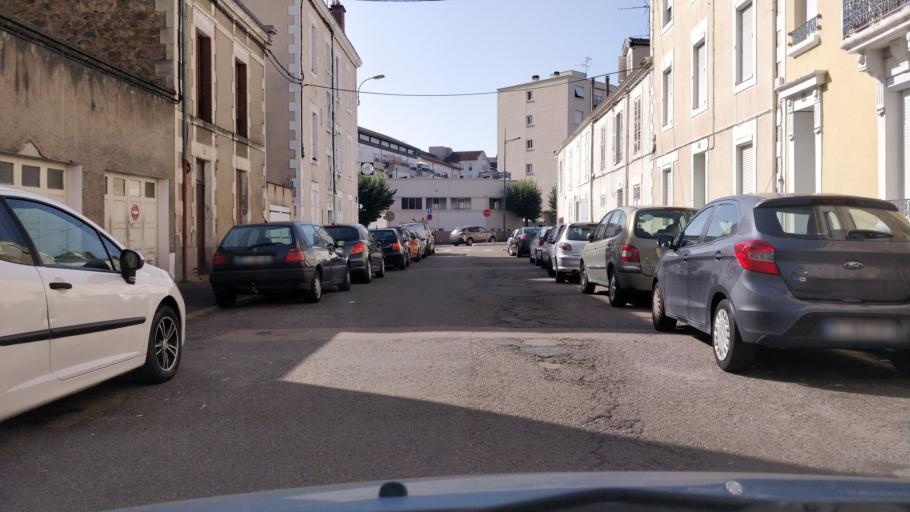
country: FR
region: Limousin
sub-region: Departement de la Haute-Vienne
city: Limoges
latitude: 45.8396
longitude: 1.2554
